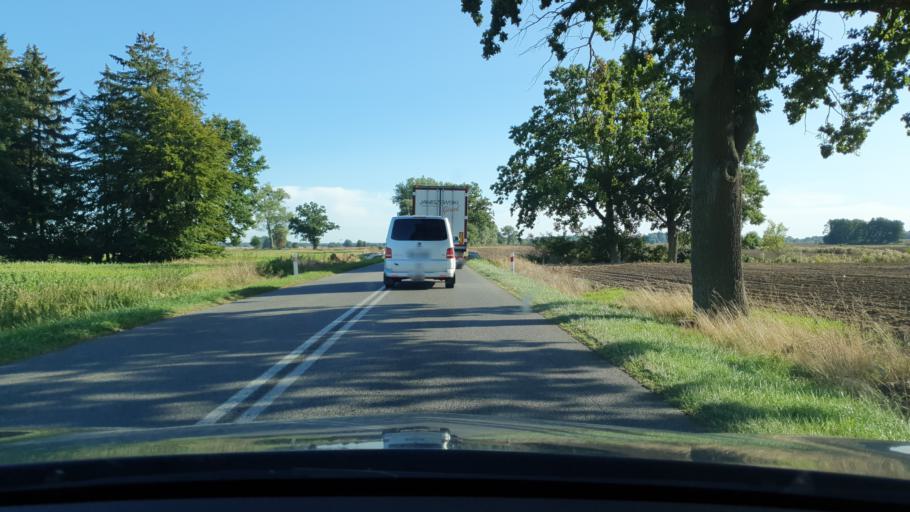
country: PL
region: West Pomeranian Voivodeship
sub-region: Powiat kamienski
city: Golczewo
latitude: 53.8267
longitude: 14.9295
